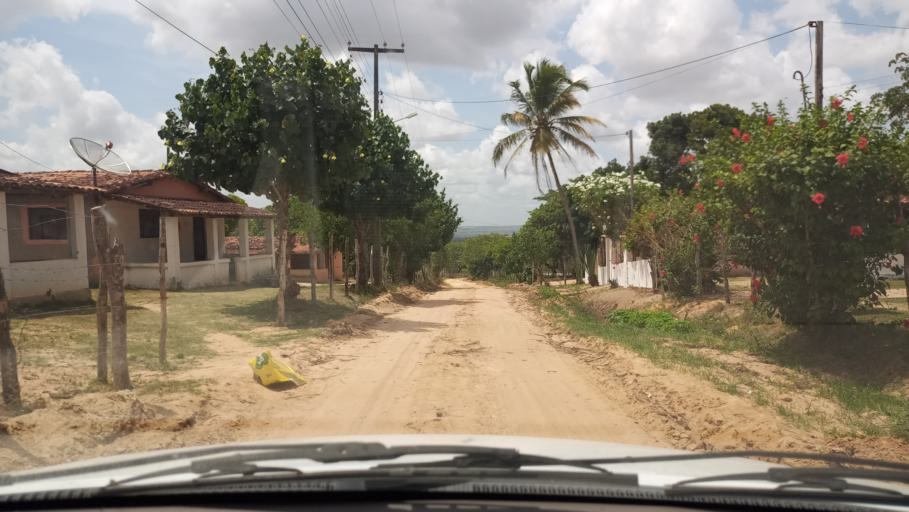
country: BR
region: Rio Grande do Norte
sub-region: Brejinho
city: Brejinho
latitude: -6.2504
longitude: -35.3368
